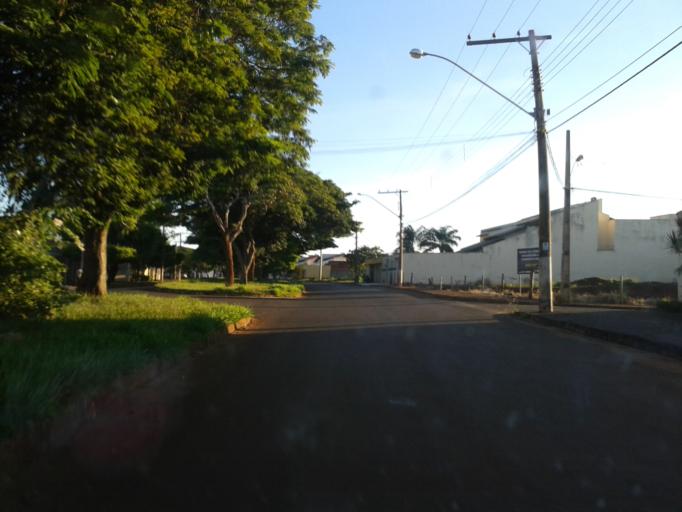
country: BR
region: Minas Gerais
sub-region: Ituiutaba
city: Ituiutaba
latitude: -18.9757
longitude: -49.4847
